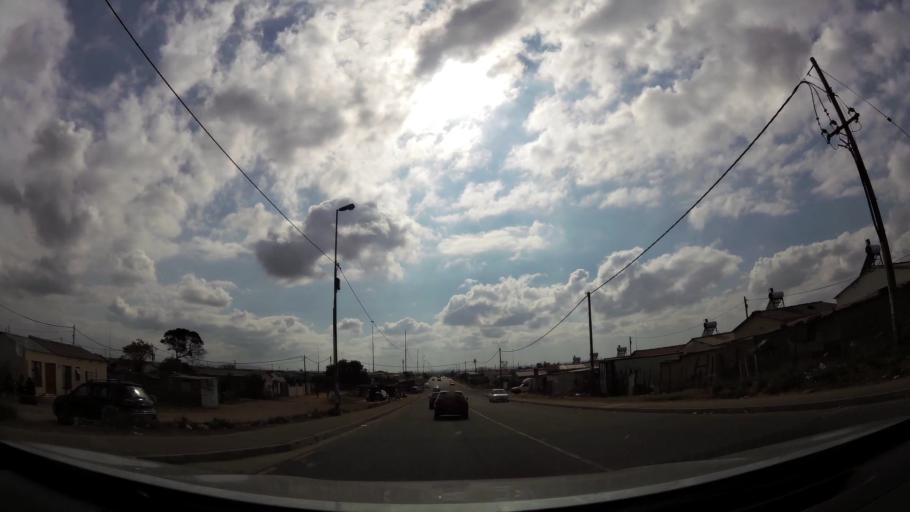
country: ZA
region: Eastern Cape
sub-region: Nelson Mandela Bay Metropolitan Municipality
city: Port Elizabeth
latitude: -33.7959
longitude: 25.5830
